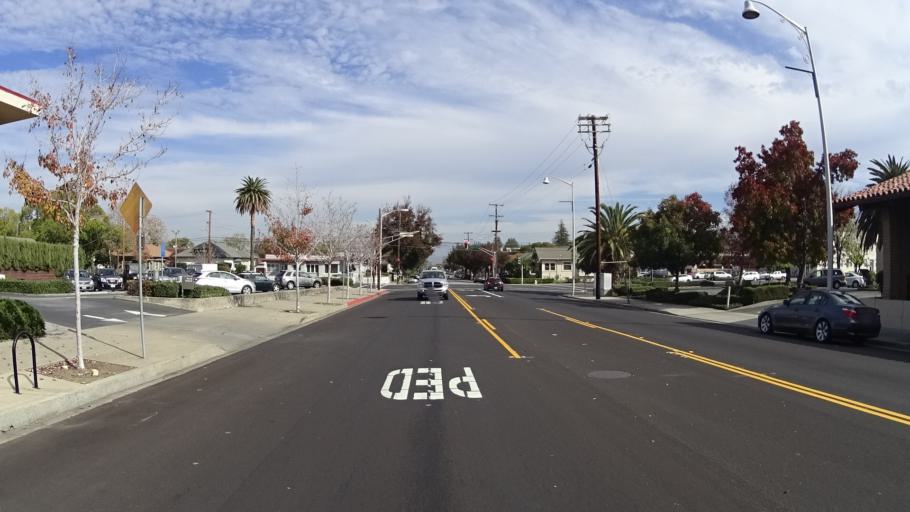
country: US
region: California
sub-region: Santa Clara County
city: Santa Clara
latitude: 37.3509
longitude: -121.9447
